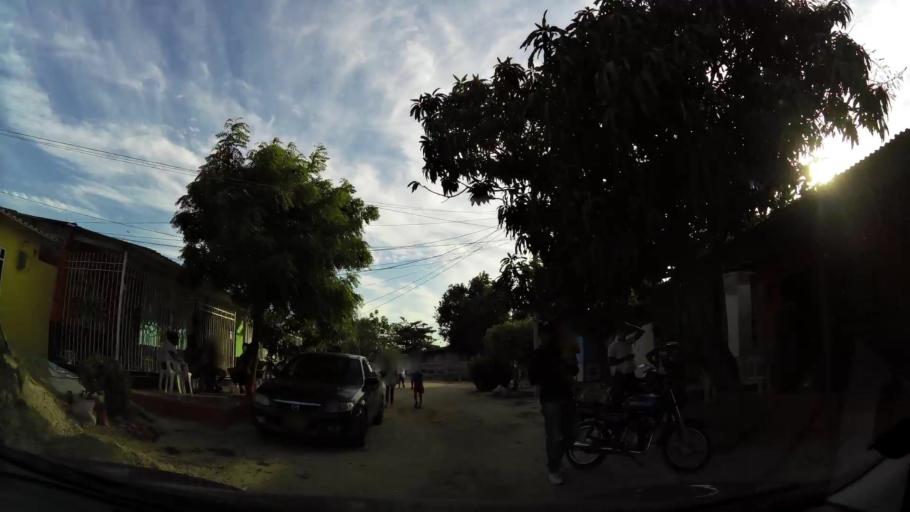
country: CO
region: Atlantico
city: Barranquilla
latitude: 10.9427
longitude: -74.8191
